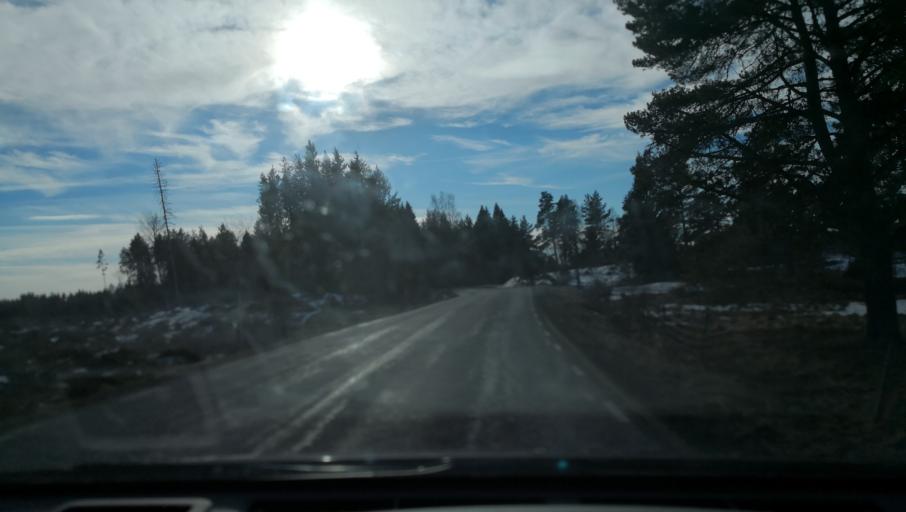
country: SE
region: Uppsala
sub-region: Osthammars Kommun
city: Osterbybruk
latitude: 60.2496
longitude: 17.9420
